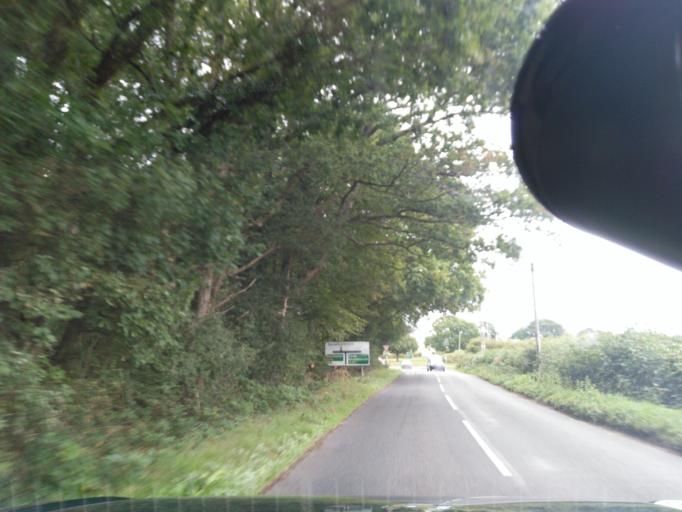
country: GB
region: England
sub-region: Dorset
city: Lytchett Matravers
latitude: 50.7426
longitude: -2.1240
